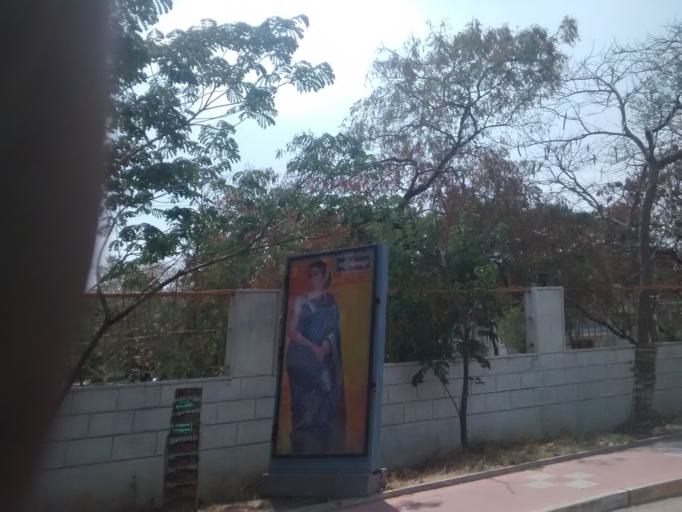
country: IN
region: Tamil Nadu
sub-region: Coimbatore
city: Singanallur
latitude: 11.0298
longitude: 77.0273
